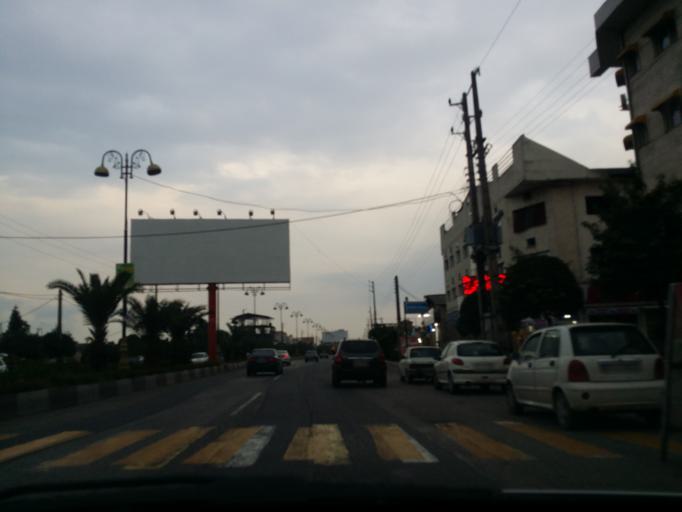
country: IR
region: Mazandaran
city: `Abbasabad
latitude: 36.7273
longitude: 51.1126
